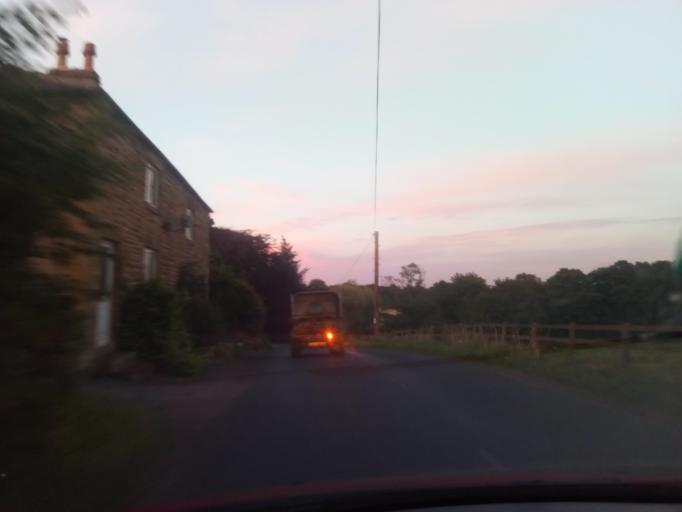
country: GB
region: England
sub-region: Northumberland
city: Warden
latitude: 54.9879
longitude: -2.2221
